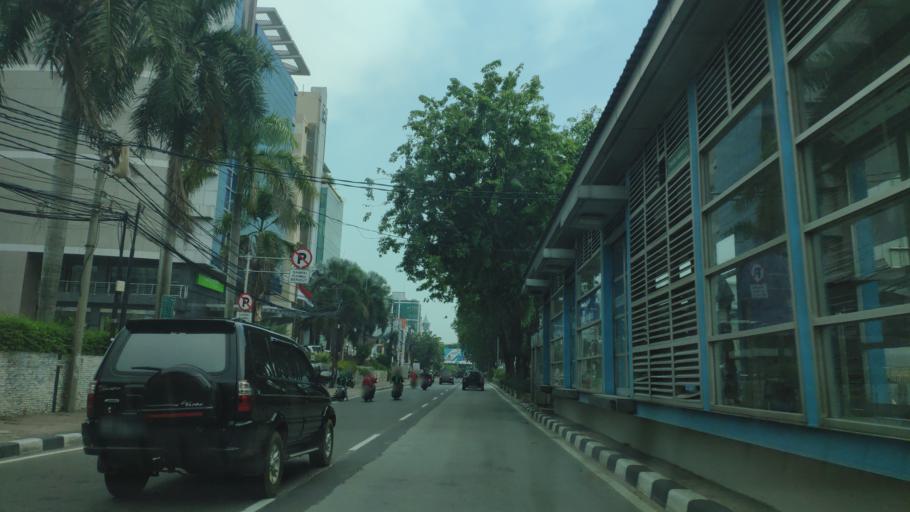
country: ID
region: Jakarta Raya
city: Jakarta
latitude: -6.1769
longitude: 106.8003
